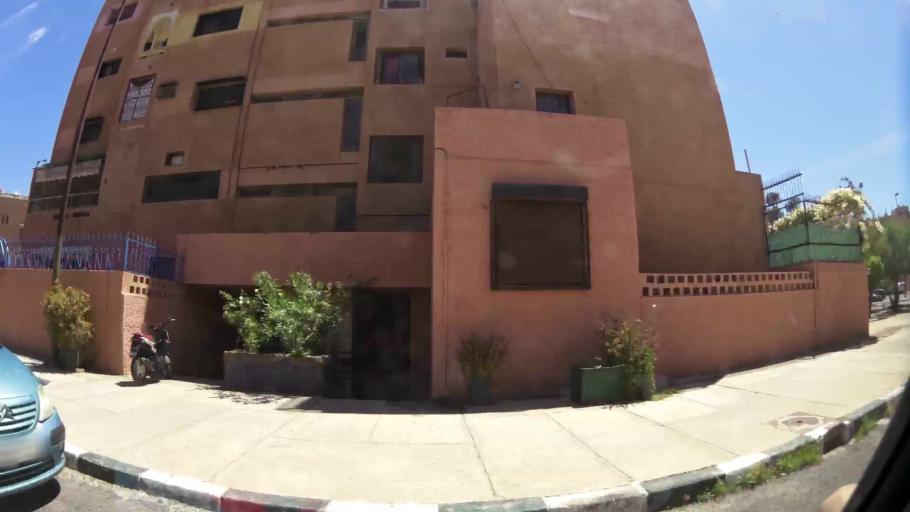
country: MA
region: Marrakech-Tensift-Al Haouz
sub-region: Marrakech
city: Marrakesh
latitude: 31.6468
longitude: -7.9998
